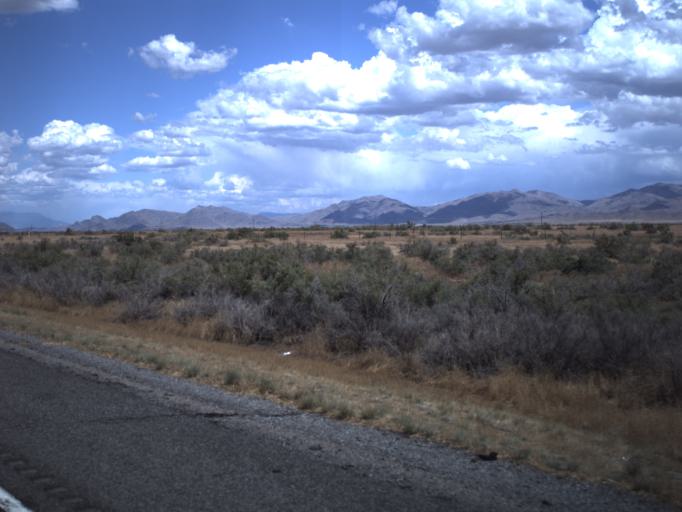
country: US
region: Utah
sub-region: Millard County
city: Delta
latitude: 39.4483
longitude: -112.4475
